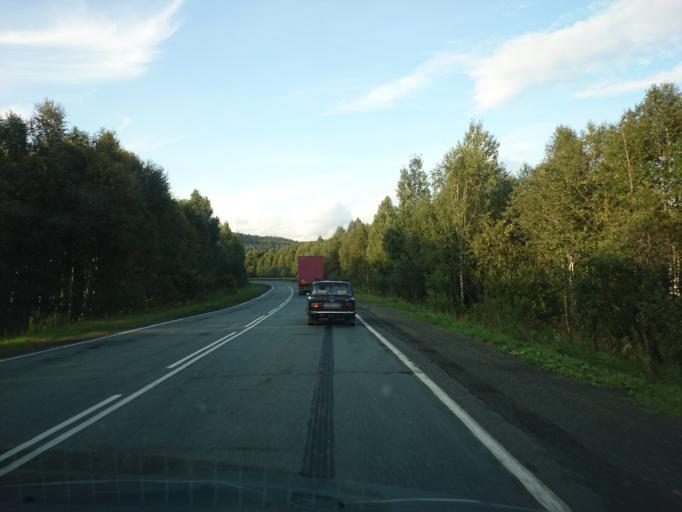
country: RU
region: Bashkortostan
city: Inzer
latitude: 53.9671
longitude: 57.8746
